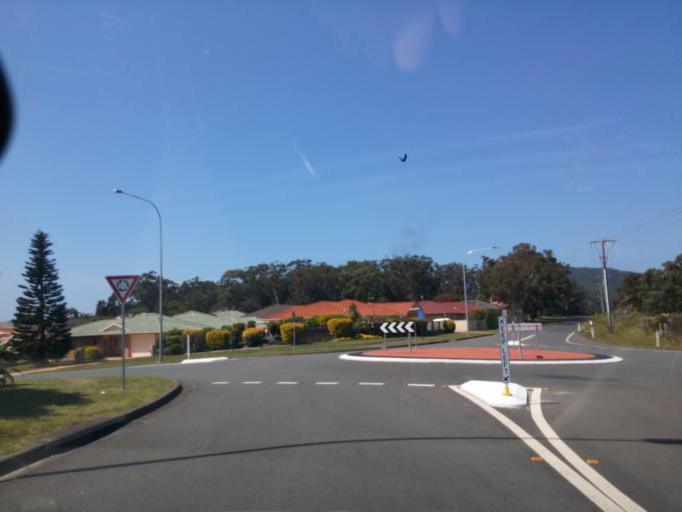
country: AU
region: New South Wales
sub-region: Great Lakes
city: Forster
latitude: -32.2132
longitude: 152.5328
